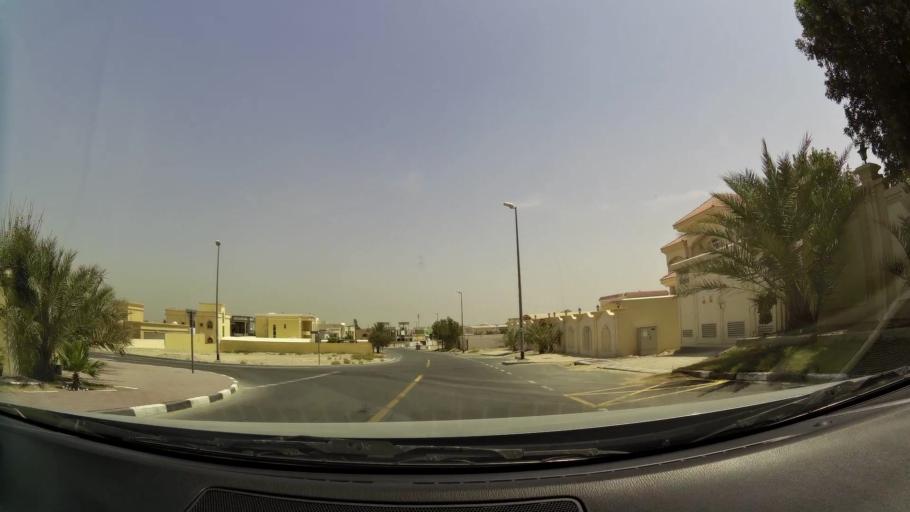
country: AE
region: Ash Shariqah
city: Sharjah
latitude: 25.1903
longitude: 55.4142
